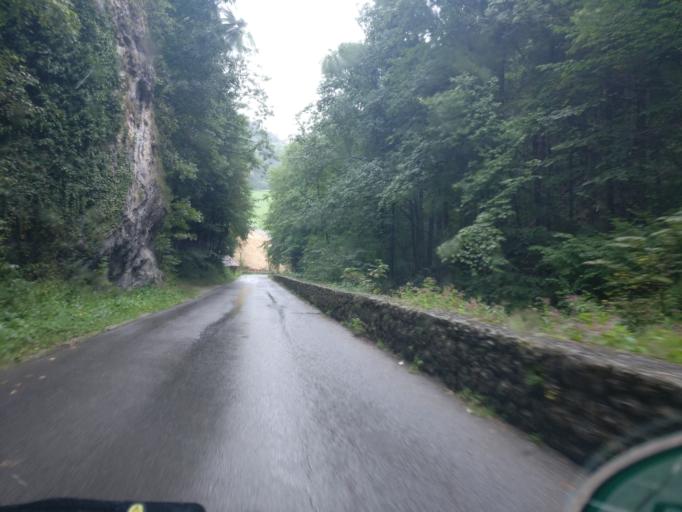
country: AT
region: Lower Austria
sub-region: Politischer Bezirk Neunkirchen
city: Schottwien
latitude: 47.6590
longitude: 15.8577
